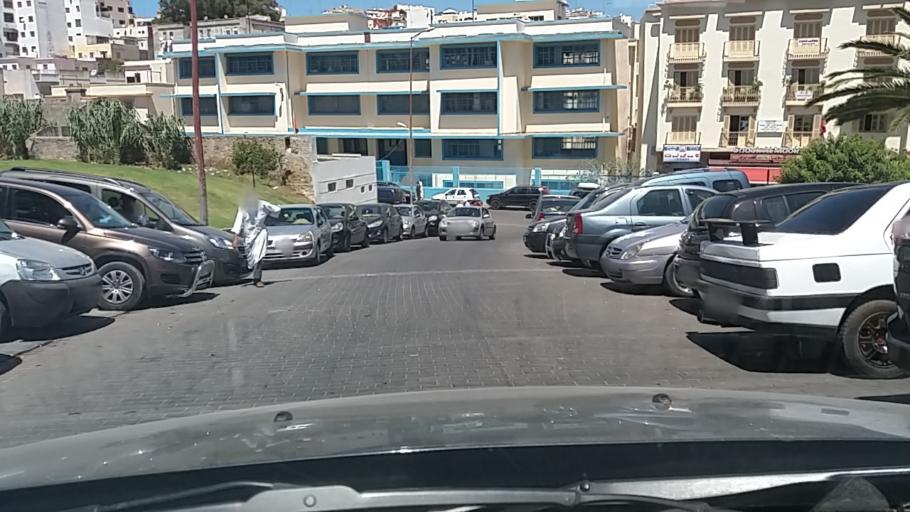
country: MA
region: Tanger-Tetouan
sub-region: Tanger-Assilah
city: Tangier
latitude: 35.7852
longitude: -5.8148
